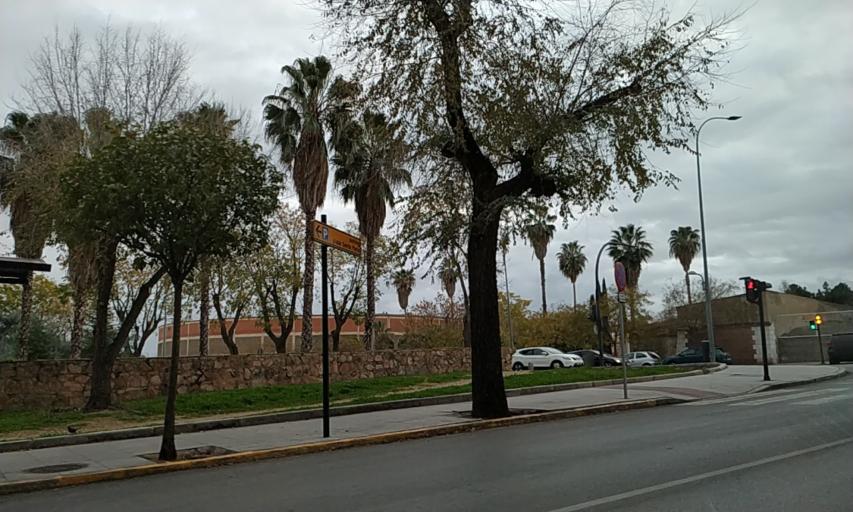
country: ES
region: Extremadura
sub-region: Provincia de Badajoz
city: Badajoz
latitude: 38.8772
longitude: -6.9651
